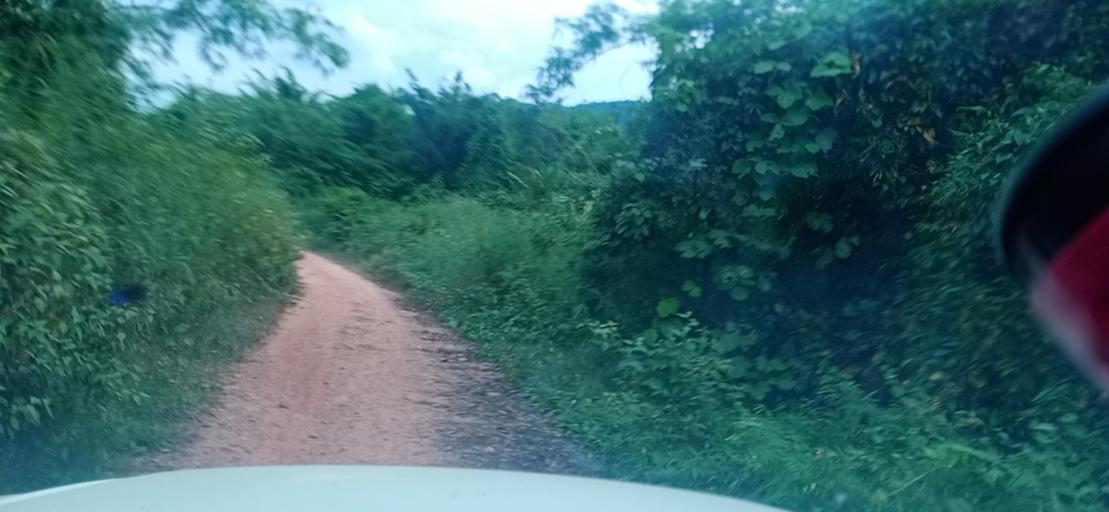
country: TH
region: Changwat Bueng Kan
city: Pak Khat
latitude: 18.5619
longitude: 103.2883
